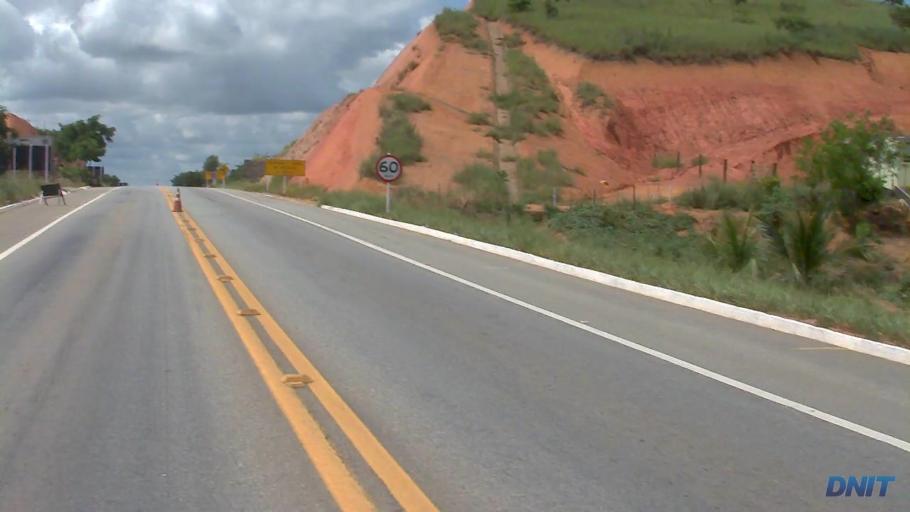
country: BR
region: Minas Gerais
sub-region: Governador Valadares
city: Governador Valadares
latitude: -18.9164
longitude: -42.0121
